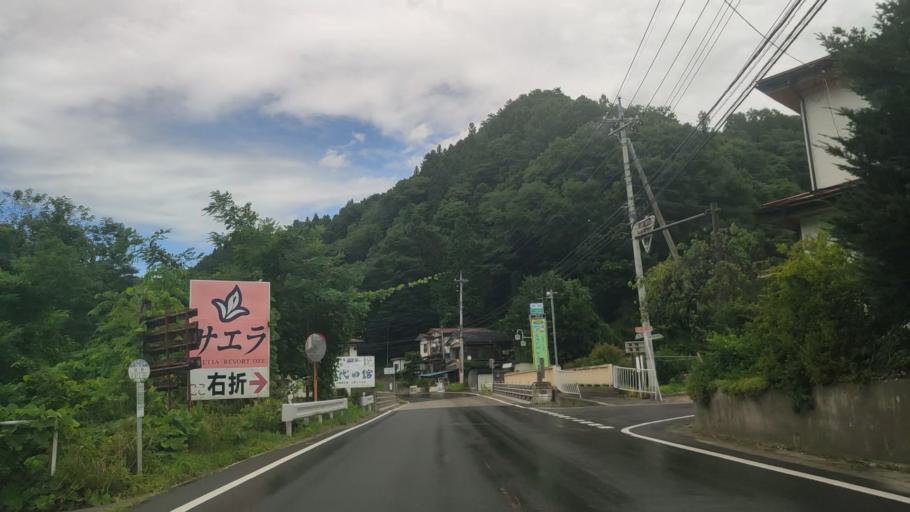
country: JP
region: Gunma
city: Numata
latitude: 36.7425
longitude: 139.2331
